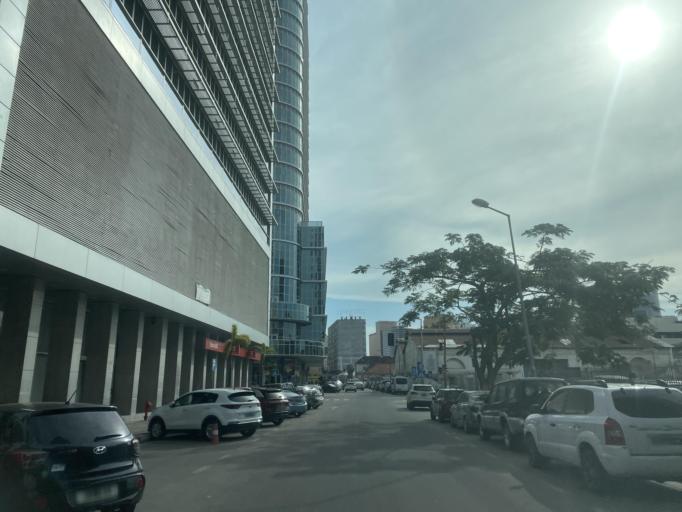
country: AO
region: Luanda
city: Luanda
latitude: -8.8095
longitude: 13.2385
